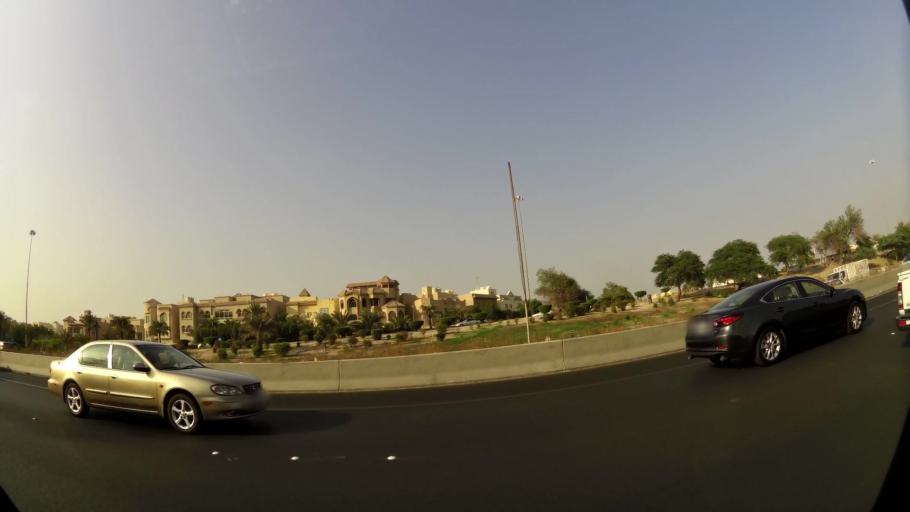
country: KW
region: Muhafazat Hawalli
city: Hawalli
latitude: 29.3052
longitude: 47.9984
